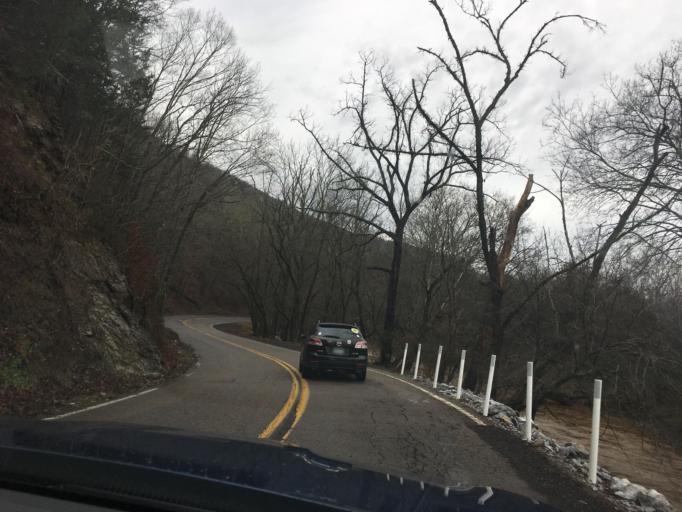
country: US
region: Tennessee
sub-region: McMinn County
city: Englewood
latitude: 35.3561
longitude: -84.4160
